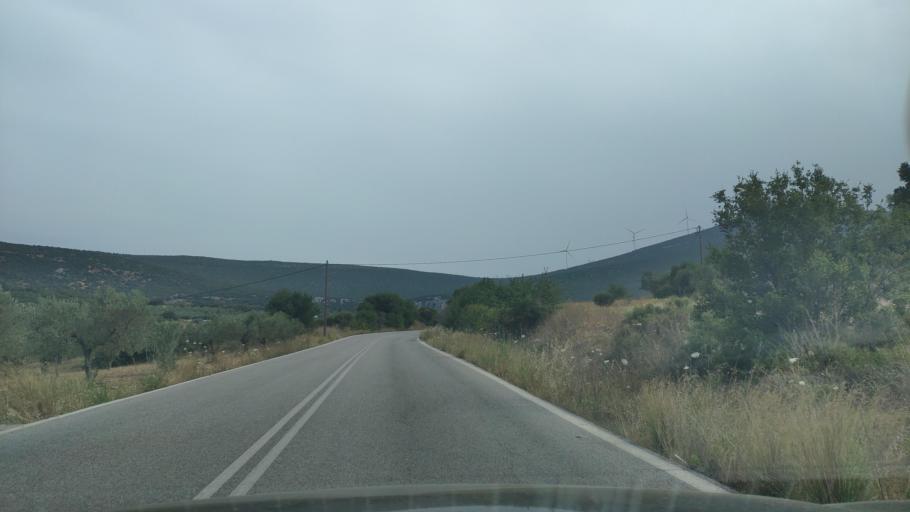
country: GR
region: Peloponnese
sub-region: Nomos Argolidos
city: Didyma
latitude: 37.5150
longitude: 23.1762
